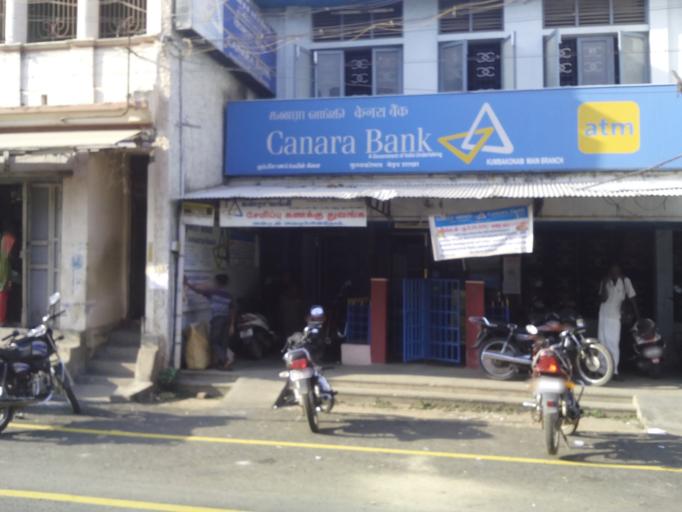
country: IN
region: Tamil Nadu
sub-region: Thanjavur
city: Kumbakonam
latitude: 10.9610
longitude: 79.3760
